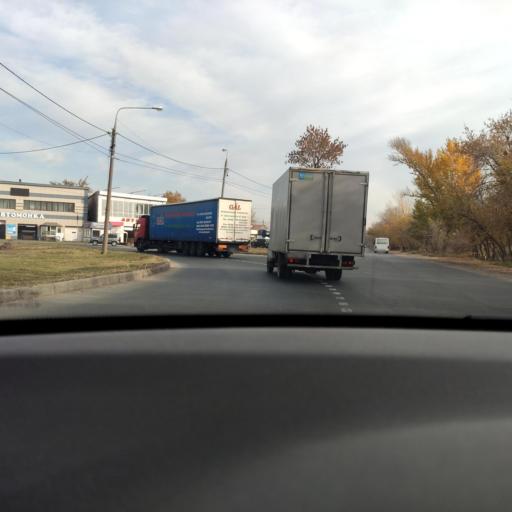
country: RU
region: Samara
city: Smyshlyayevka
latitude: 53.2323
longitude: 50.3079
